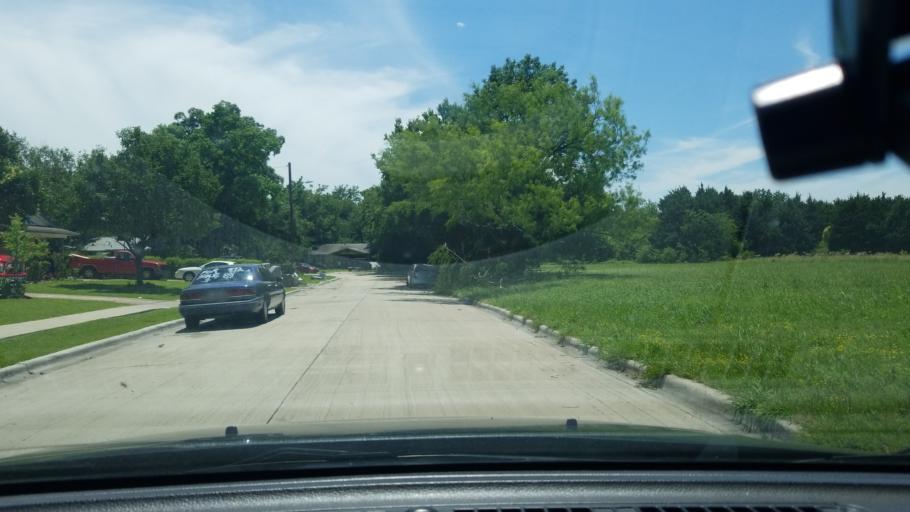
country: US
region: Texas
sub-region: Dallas County
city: Mesquite
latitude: 32.7828
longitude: -96.6217
